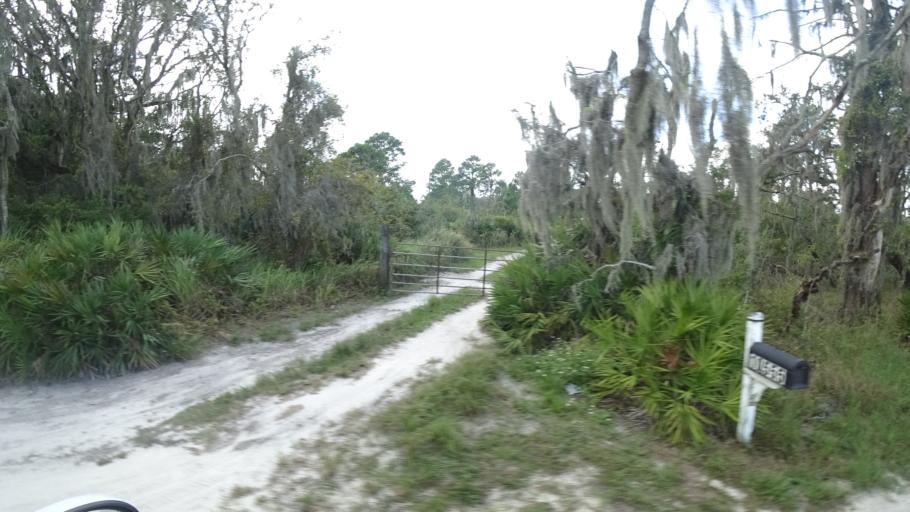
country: US
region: Florida
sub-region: Hillsborough County
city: Wimauma
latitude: 27.6077
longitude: -82.2107
